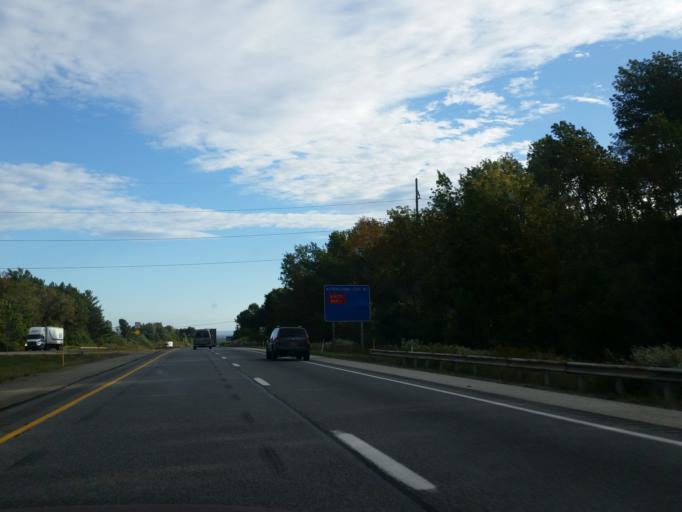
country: US
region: Pennsylvania
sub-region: Erie County
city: North East
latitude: 42.1783
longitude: -79.8411
